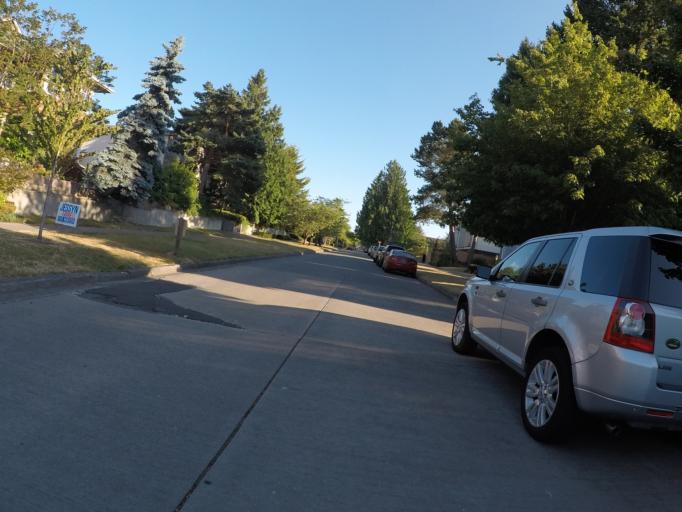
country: US
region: Washington
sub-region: King County
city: Seattle
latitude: 47.5902
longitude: -122.3876
